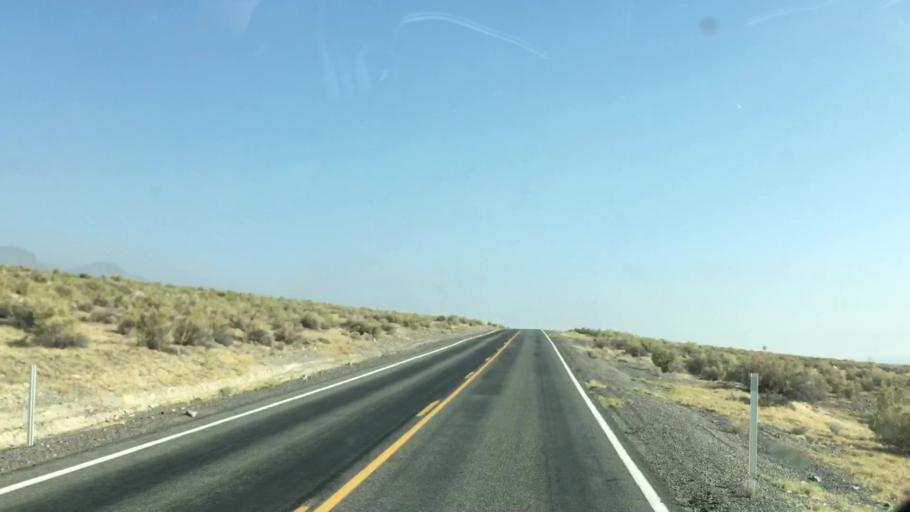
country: US
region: Nevada
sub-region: Lyon County
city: Fernley
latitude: 39.9725
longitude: -119.3837
